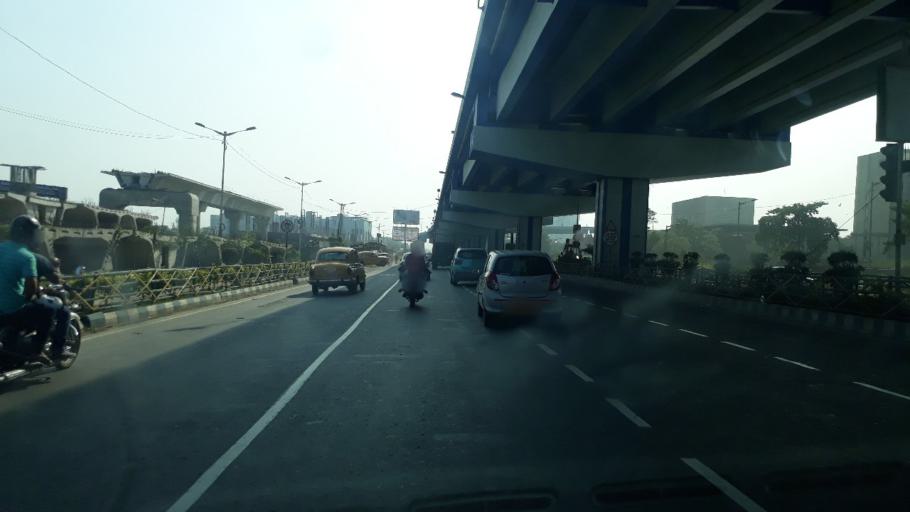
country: IN
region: West Bengal
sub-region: Kolkata
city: Kolkata
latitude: 22.5465
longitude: 88.3995
